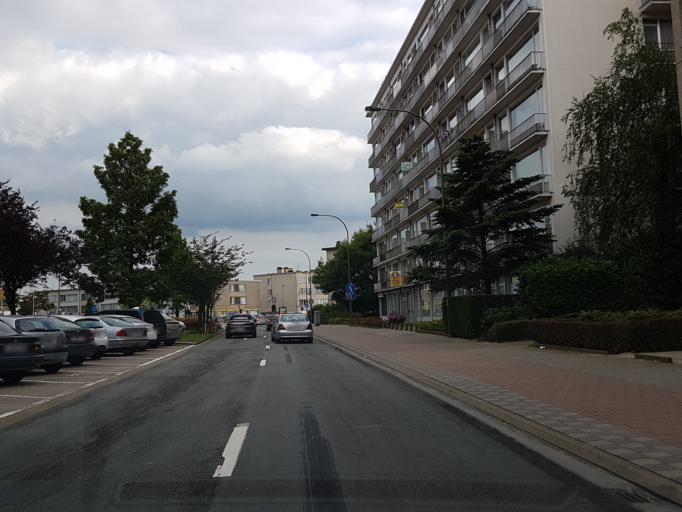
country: BE
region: Flanders
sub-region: Provincie Antwerpen
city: Antwerpen
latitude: 51.2559
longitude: 4.4344
